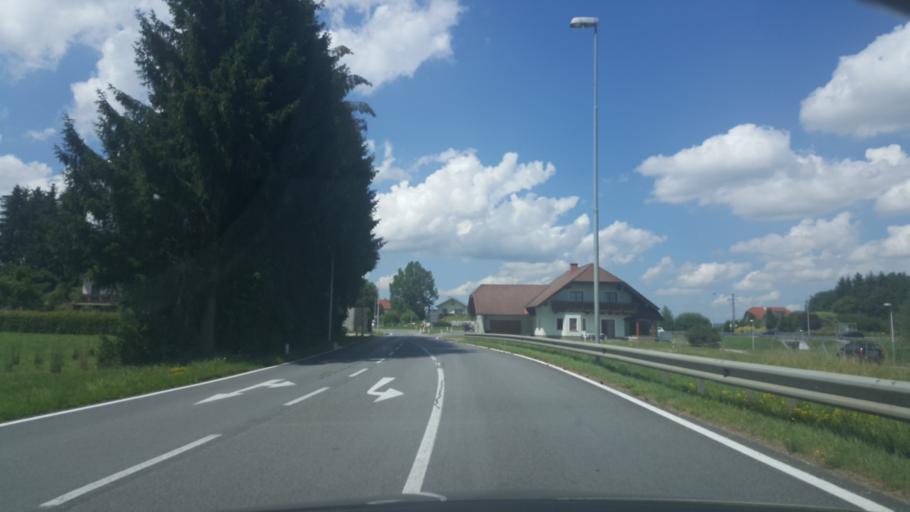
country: AT
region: Upper Austria
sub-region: Politischer Bezirk Vocklabruck
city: Gampern
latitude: 48.0015
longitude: 13.5455
